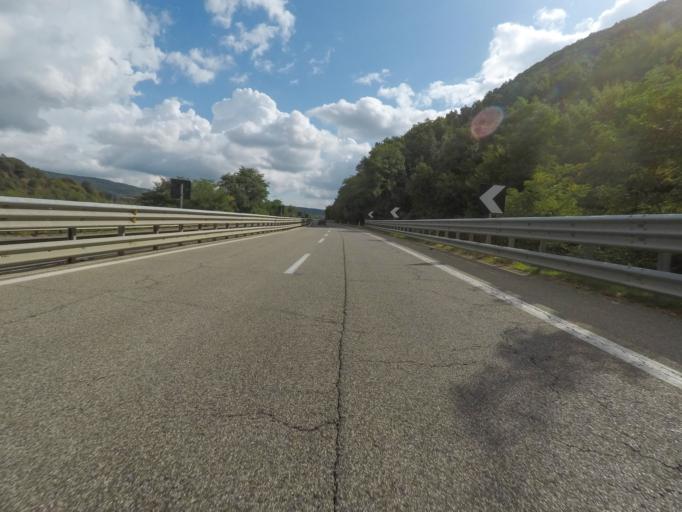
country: IT
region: Tuscany
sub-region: Provincia di Siena
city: Rapolano Terme
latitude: 43.2896
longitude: 11.6155
